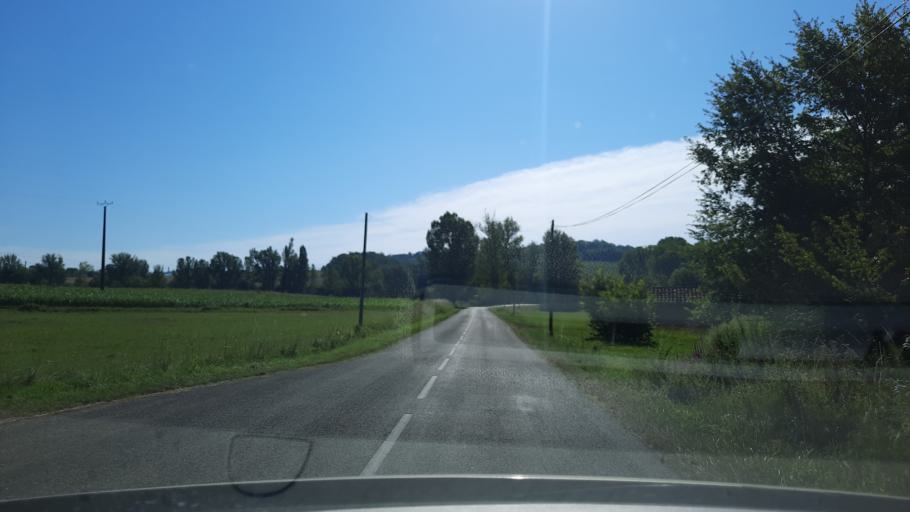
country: FR
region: Midi-Pyrenees
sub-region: Departement du Tarn-et-Garonne
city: Realville
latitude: 44.1917
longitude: 1.4513
